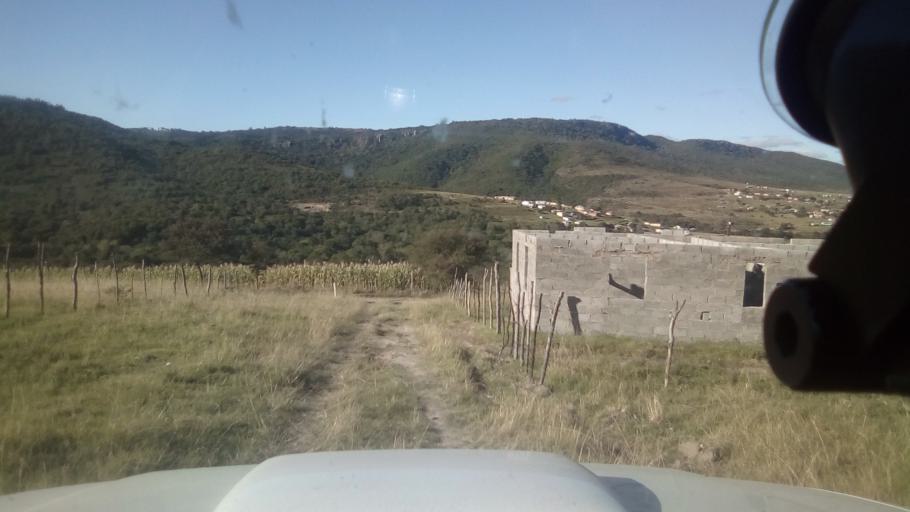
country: ZA
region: Eastern Cape
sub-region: Buffalo City Metropolitan Municipality
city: Bhisho
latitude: -32.7274
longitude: 27.3464
